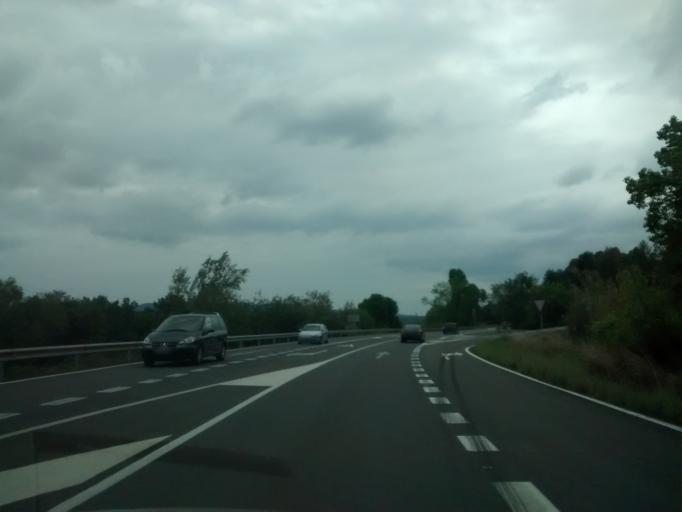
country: ES
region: Catalonia
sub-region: Provincia de Tarragona
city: Tortosa
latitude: 40.8574
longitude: 0.5118
